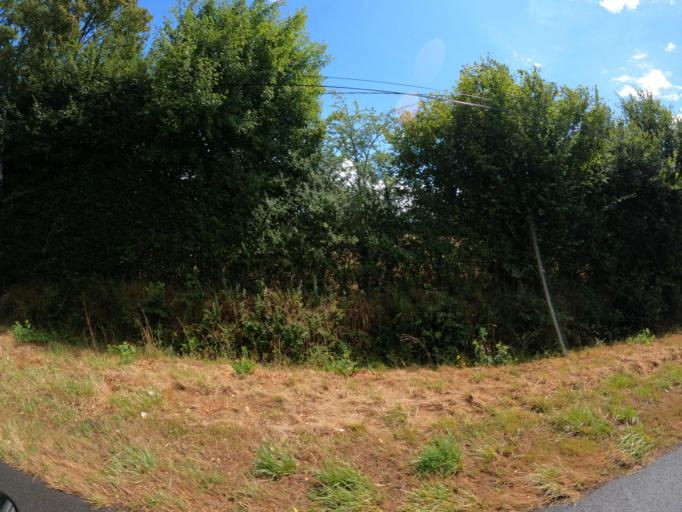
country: FR
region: Pays de la Loire
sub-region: Departement de Maine-et-Loire
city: Feneu
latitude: 47.5919
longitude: -0.5894
